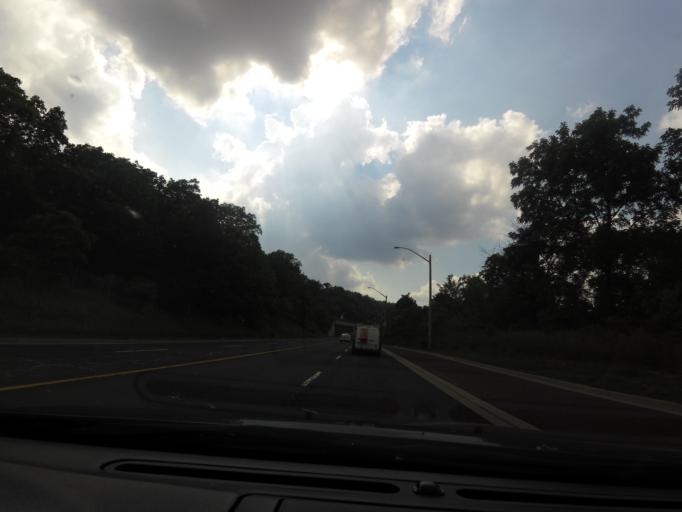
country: CA
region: Ontario
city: Hamilton
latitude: 43.2339
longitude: -79.8234
